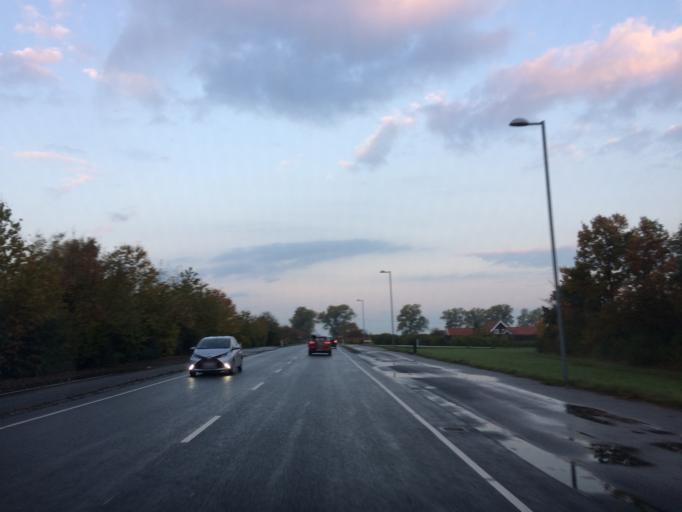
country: DK
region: Zealand
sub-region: Ringsted Kommune
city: Ringsted
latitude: 55.4606
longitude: 11.7804
